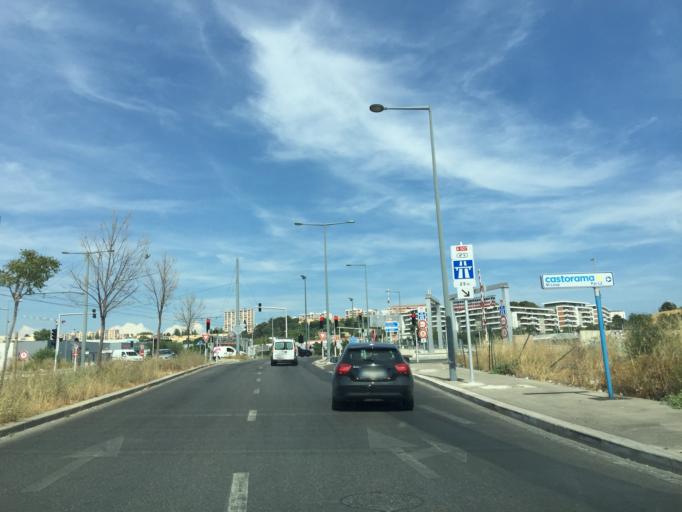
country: FR
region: Provence-Alpes-Cote d'Azur
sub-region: Departement des Bouches-du-Rhone
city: Marseille 12
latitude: 43.2949
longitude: 5.4235
